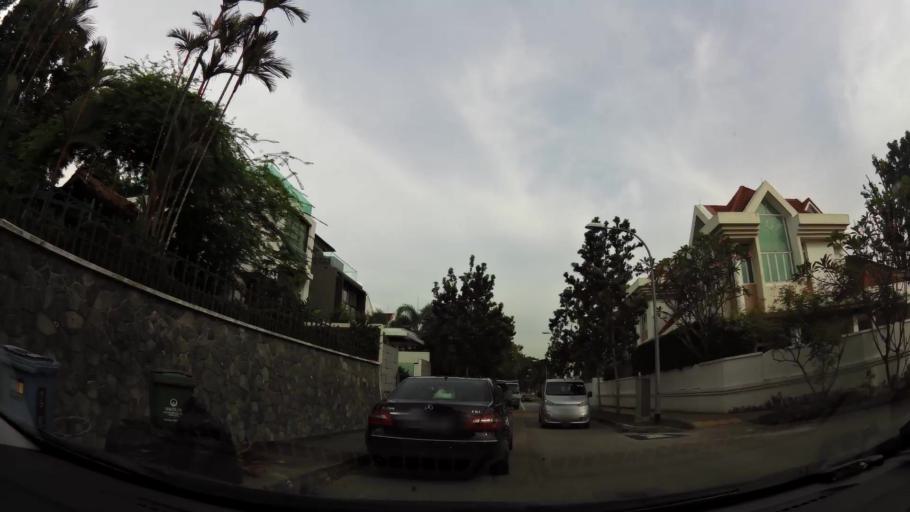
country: SG
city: Singapore
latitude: 1.3239
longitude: 103.8190
